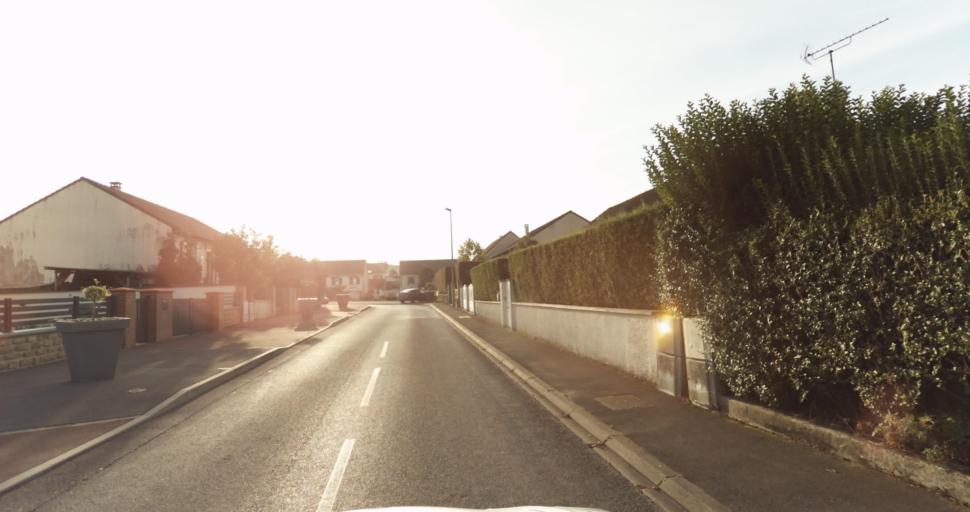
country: FR
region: Champagne-Ardenne
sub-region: Departement des Ardennes
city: Villers-Semeuse
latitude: 49.7482
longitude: 4.7425
